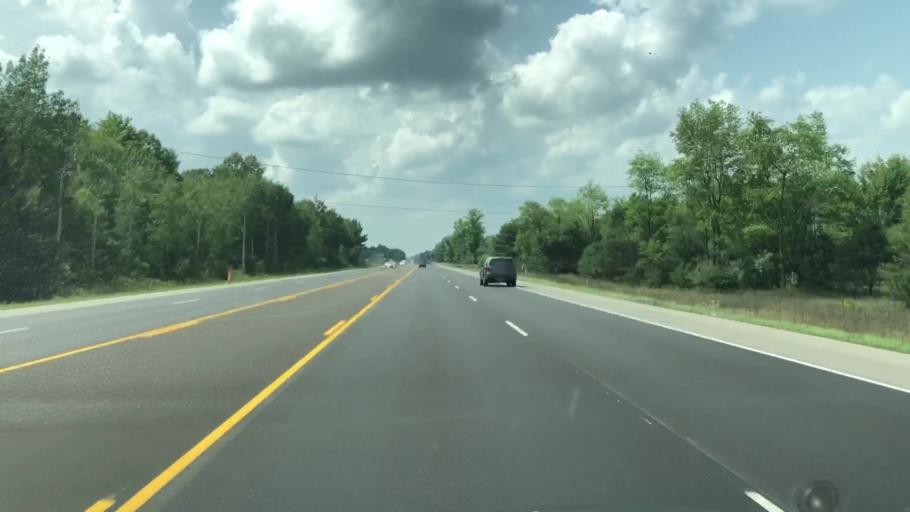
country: US
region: Michigan
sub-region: Isabella County
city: Shepherd
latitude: 43.6117
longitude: -84.6129
